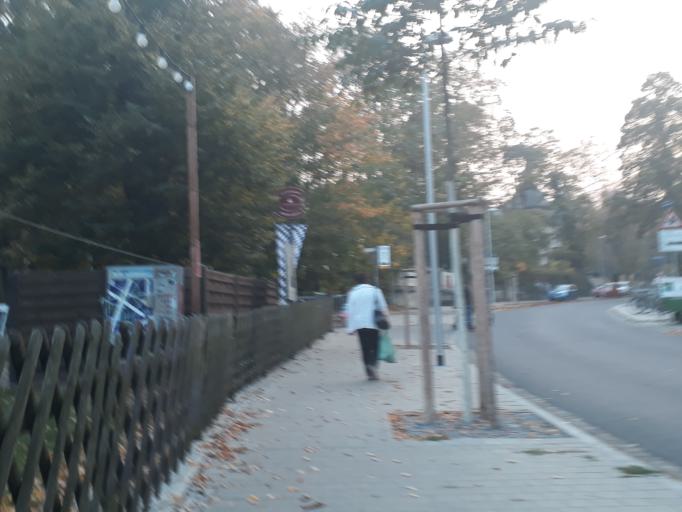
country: DE
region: Saxony
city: Heidenau
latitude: 51.0093
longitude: 13.8614
